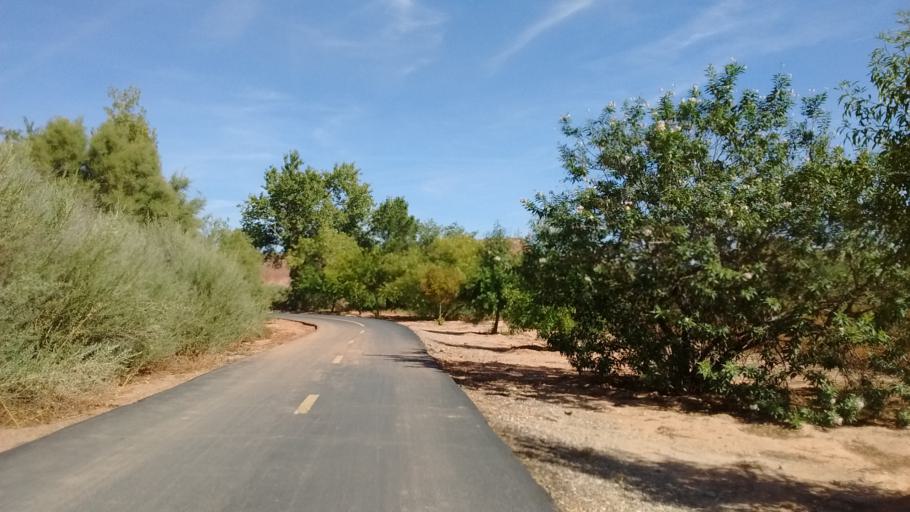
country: US
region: Utah
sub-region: Washington County
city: Saint George
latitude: 37.0590
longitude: -113.5989
